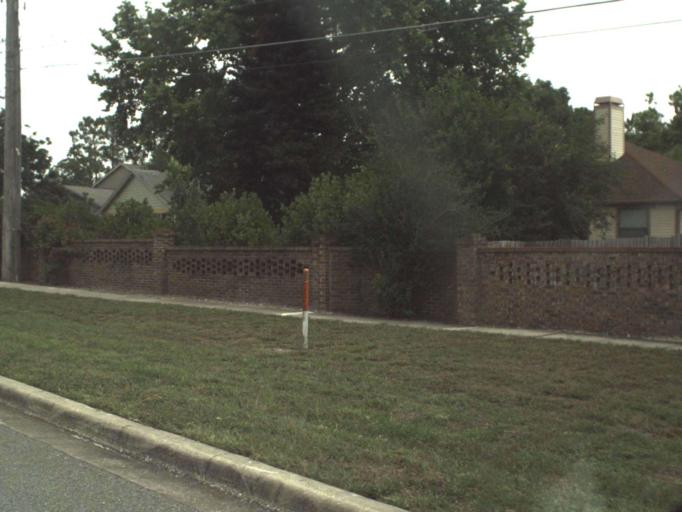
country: US
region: Florida
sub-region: Seminole County
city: Goldenrod
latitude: 28.6181
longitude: -81.2683
